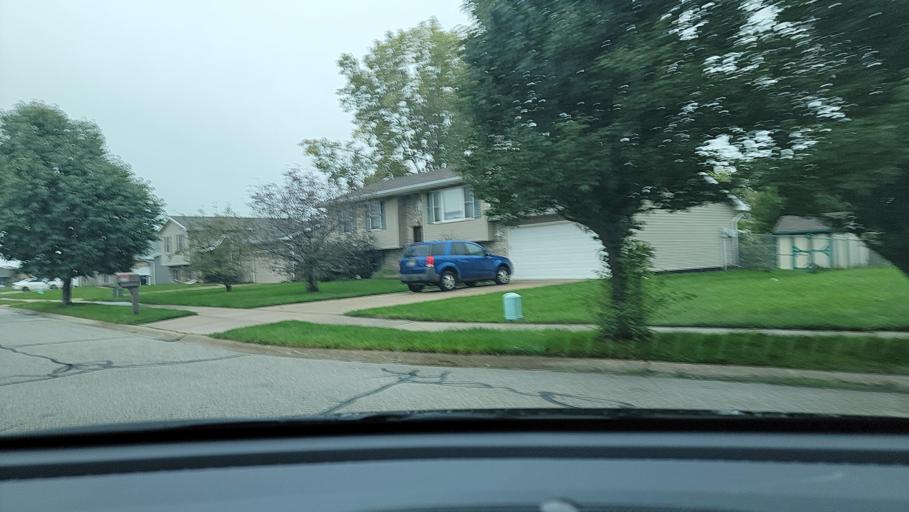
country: US
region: Indiana
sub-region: Porter County
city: Portage
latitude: 41.5451
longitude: -87.1896
